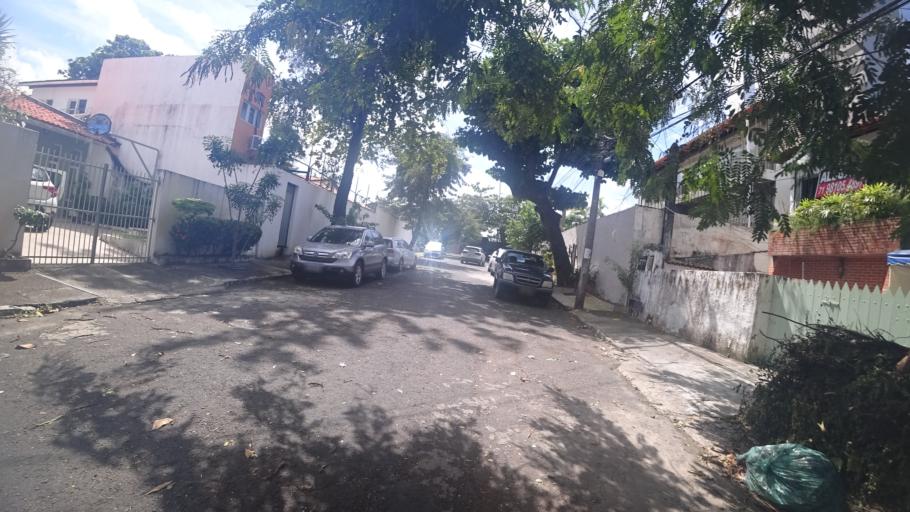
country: BR
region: Bahia
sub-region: Salvador
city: Salvador
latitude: -12.9921
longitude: -38.4574
